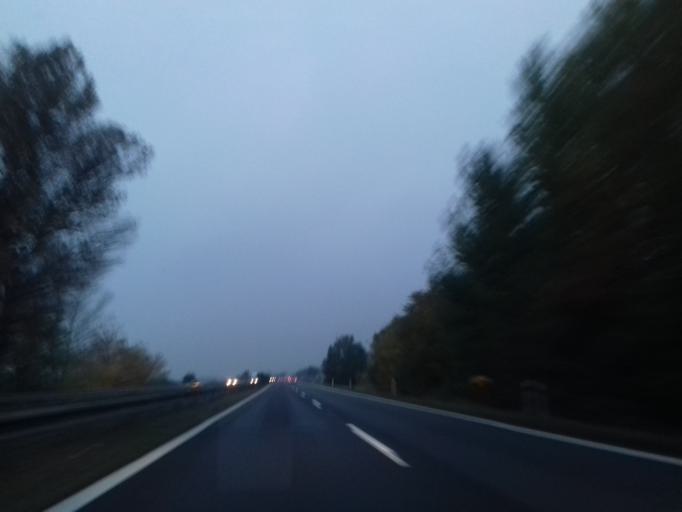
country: CZ
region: Olomoucky
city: Skrben
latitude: 49.6283
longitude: 17.1640
